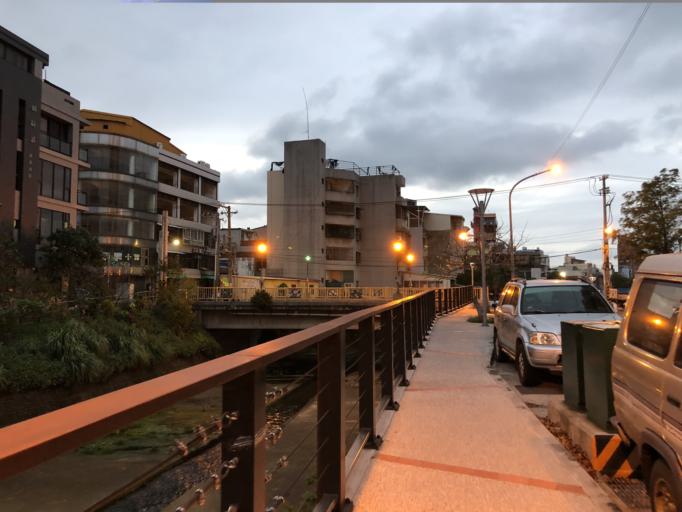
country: TW
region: Taiwan
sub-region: Hsinchu
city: Zhubei
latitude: 24.7329
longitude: 121.0911
